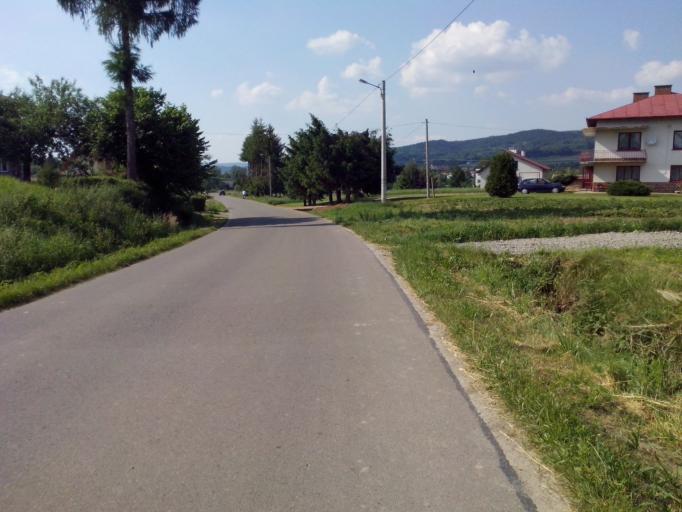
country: PL
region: Subcarpathian Voivodeship
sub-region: Powiat brzozowski
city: Blizne
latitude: 49.7455
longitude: 21.9738
